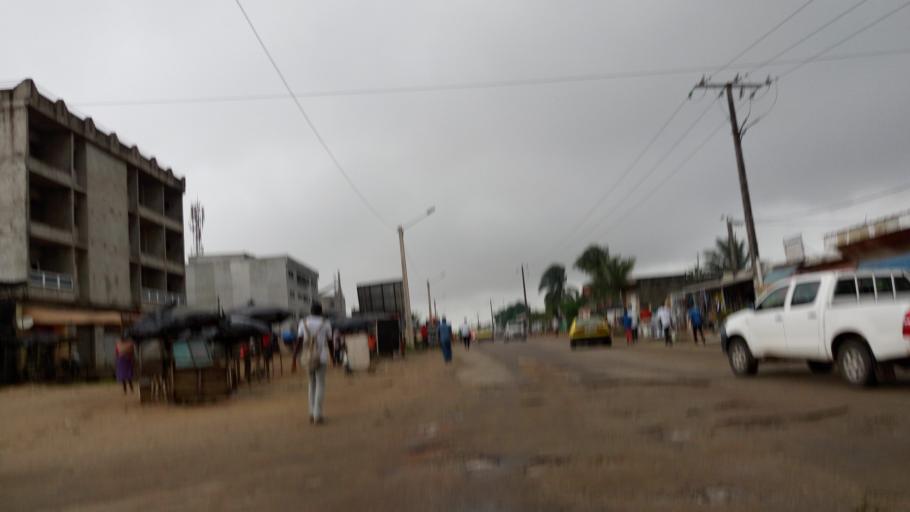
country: CI
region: Lagunes
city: Abobo
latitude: 5.4047
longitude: -3.9928
